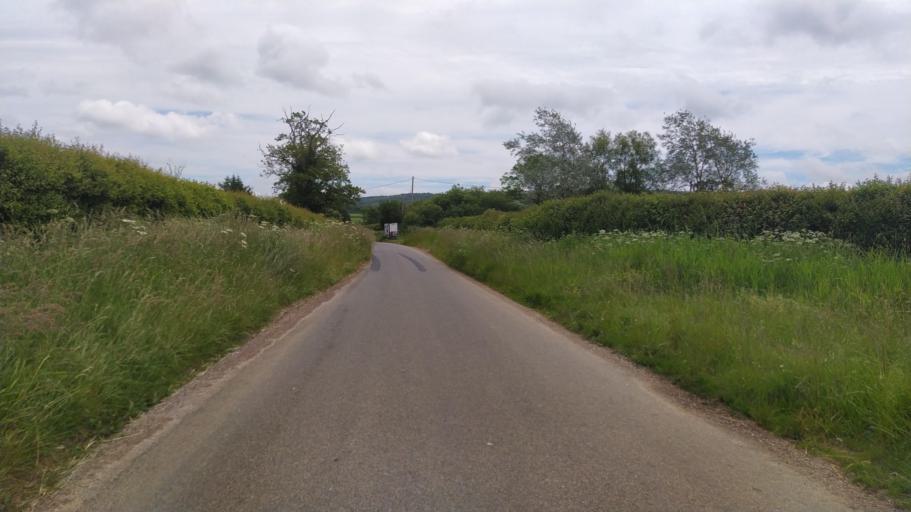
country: GB
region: England
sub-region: Dorset
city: Sturminster Newton
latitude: 50.8976
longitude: -2.2923
